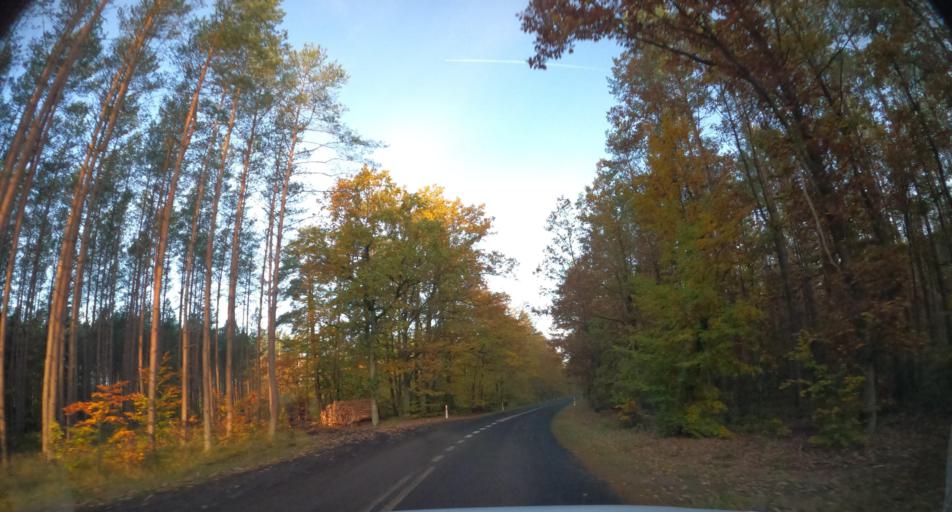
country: PL
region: West Pomeranian Voivodeship
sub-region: Powiat policki
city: Nowe Warpno
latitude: 53.6049
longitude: 14.3203
